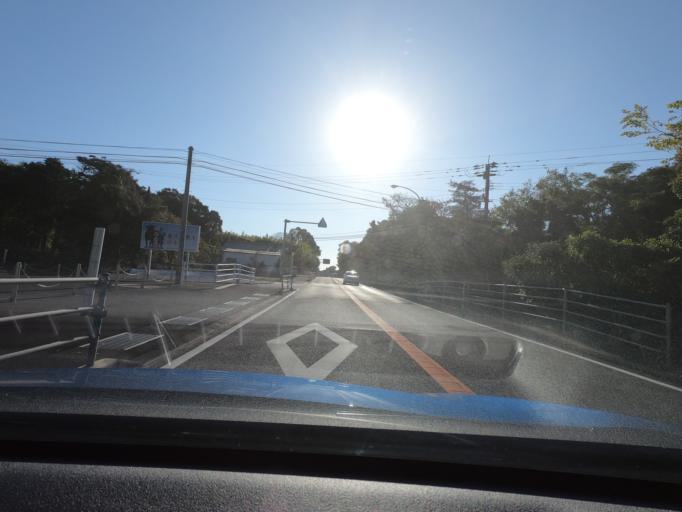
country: JP
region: Kumamoto
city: Minamata
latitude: 32.1615
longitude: 130.3671
